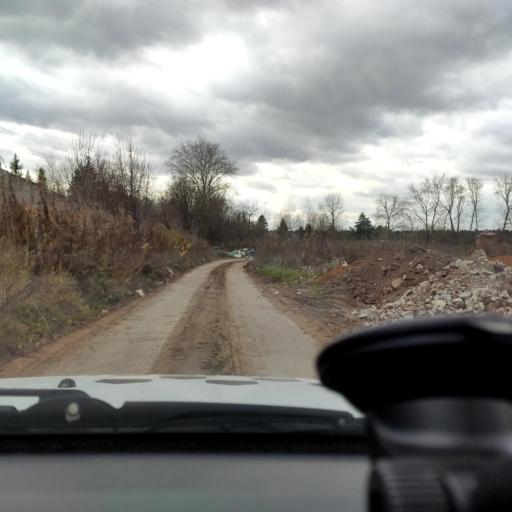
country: RU
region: Perm
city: Perm
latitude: 57.9949
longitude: 56.3322
